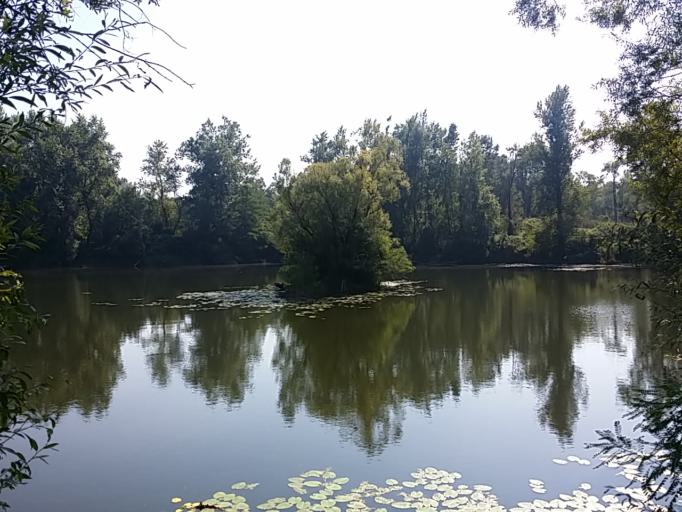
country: HR
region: Koprivnicko-Krizevacka
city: Ferdinandovac
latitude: 46.1151
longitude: 17.1994
